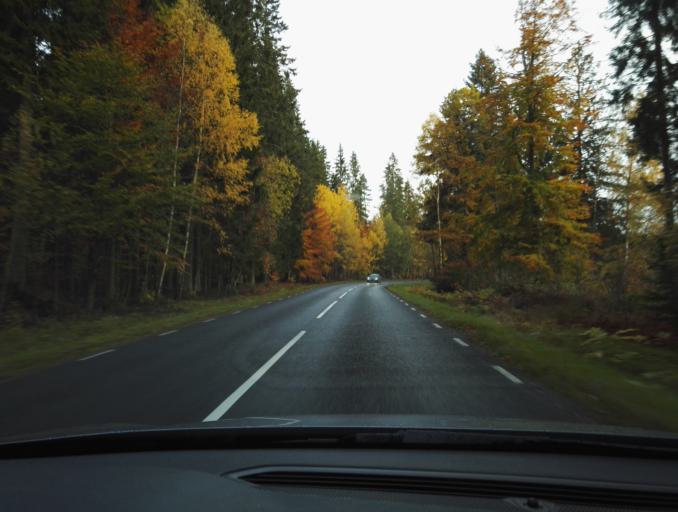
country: SE
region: Kronoberg
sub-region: Alvesta Kommun
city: Moheda
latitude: 57.0085
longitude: 14.6844
